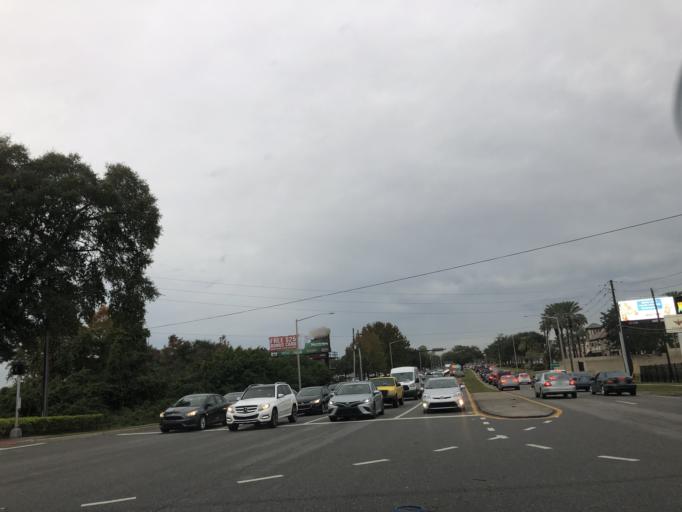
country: US
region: Florida
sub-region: Orange County
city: Doctor Phillips
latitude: 28.4500
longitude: -81.4820
